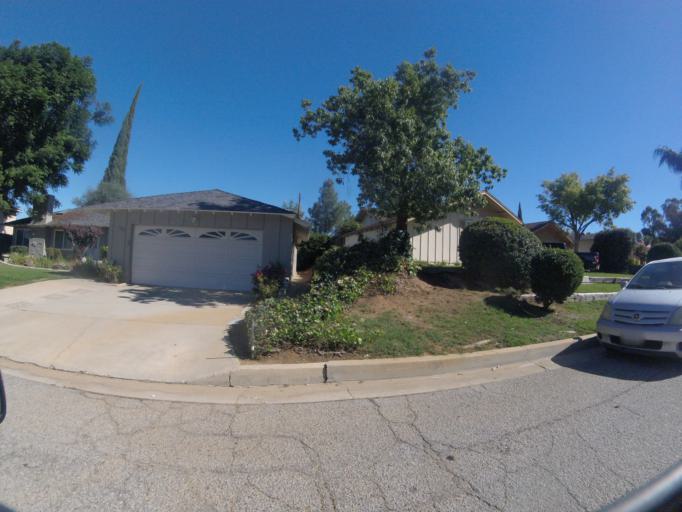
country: US
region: California
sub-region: San Bernardino County
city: Mentone
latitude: 34.0326
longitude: -117.1488
